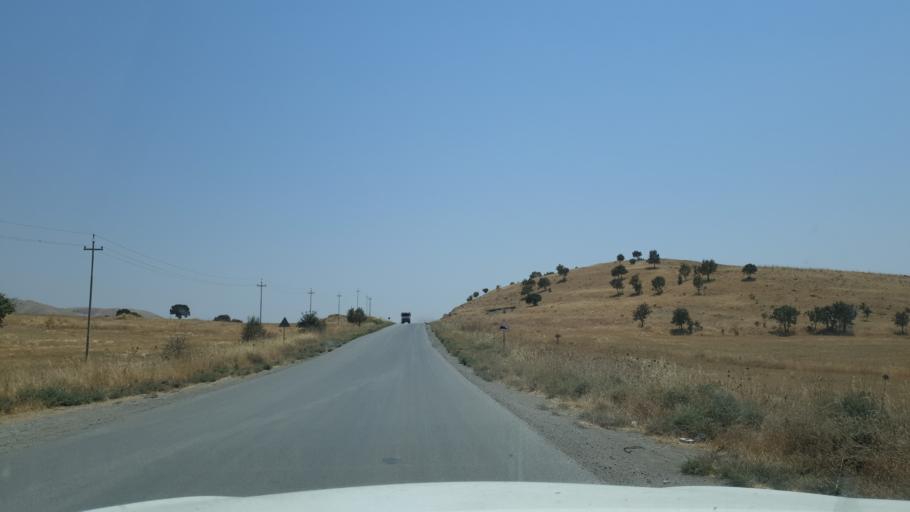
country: IQ
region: Arbil
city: Nahiyat Hiran
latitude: 36.2391
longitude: 44.5950
